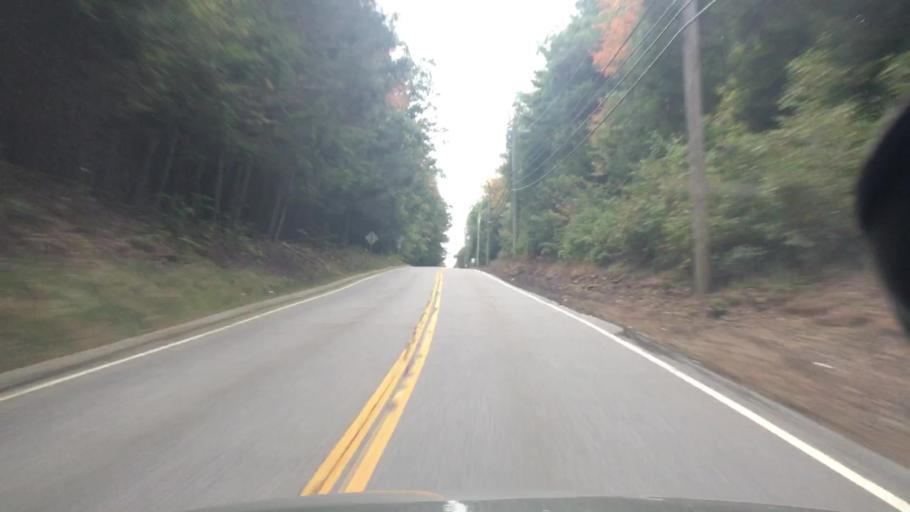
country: US
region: Connecticut
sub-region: Tolland County
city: Stafford
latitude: 41.9627
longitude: -72.2502
